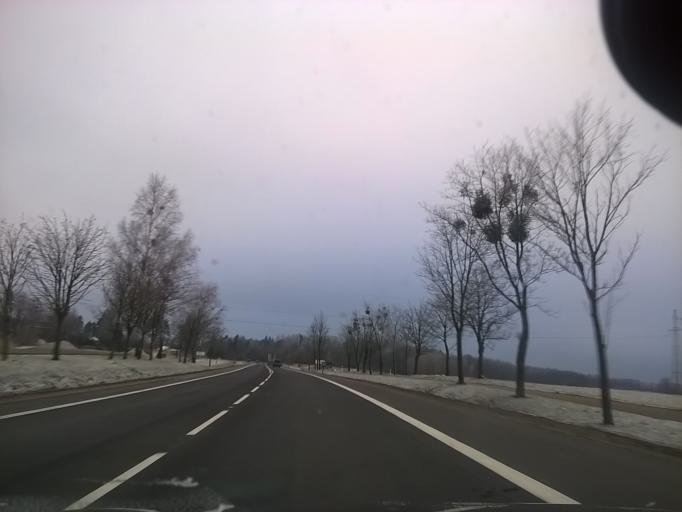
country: PL
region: Warmian-Masurian Voivodeship
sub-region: Powiat olsztynski
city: Olsztyn
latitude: 53.7860
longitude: 20.5808
